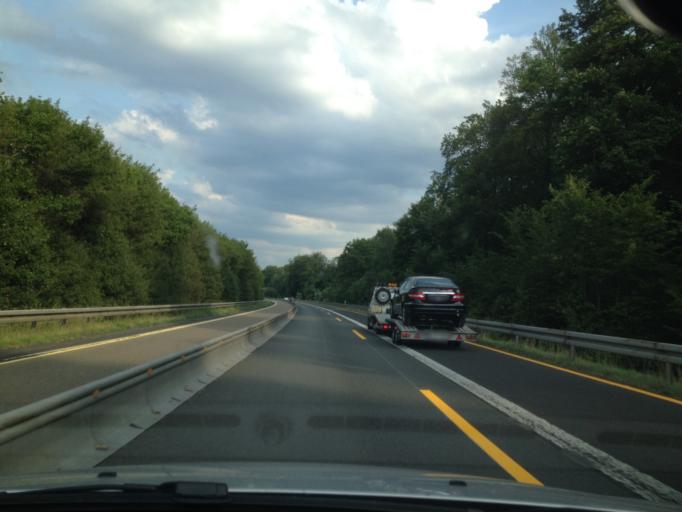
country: DE
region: Hesse
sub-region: Regierungsbezirk Darmstadt
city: Grosskrotzenburg
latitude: 50.1124
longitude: 8.9877
